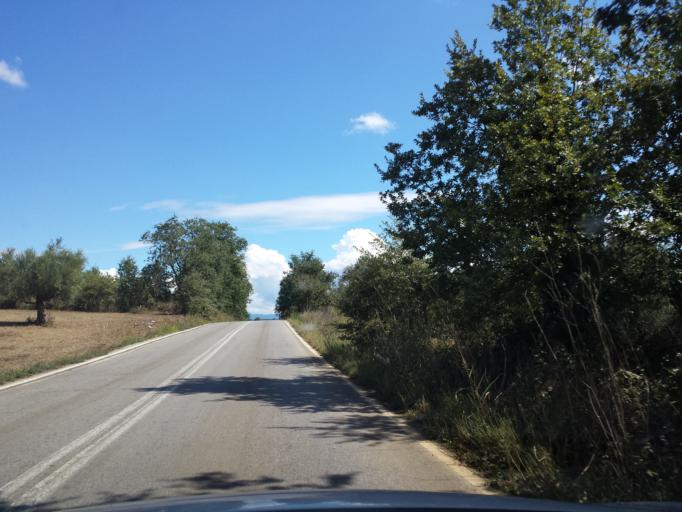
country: GR
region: Peloponnese
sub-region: Nomos Messinias
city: Vlakhopoulon
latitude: 36.9841
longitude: 21.8238
